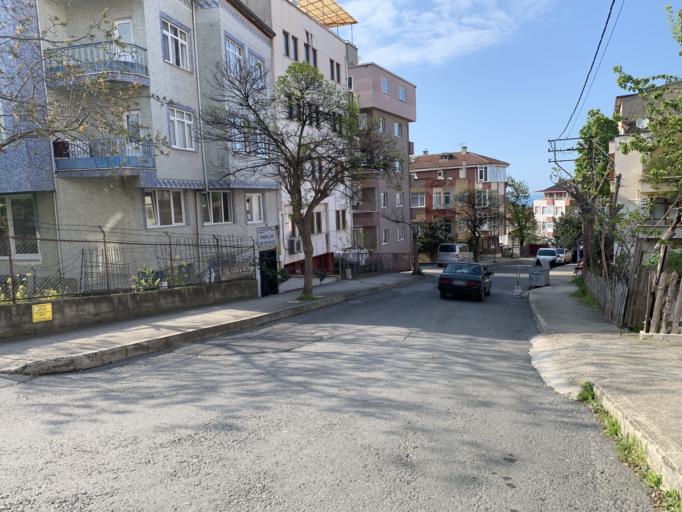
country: TR
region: Trabzon
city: Trabzon
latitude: 40.9953
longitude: 39.7609
